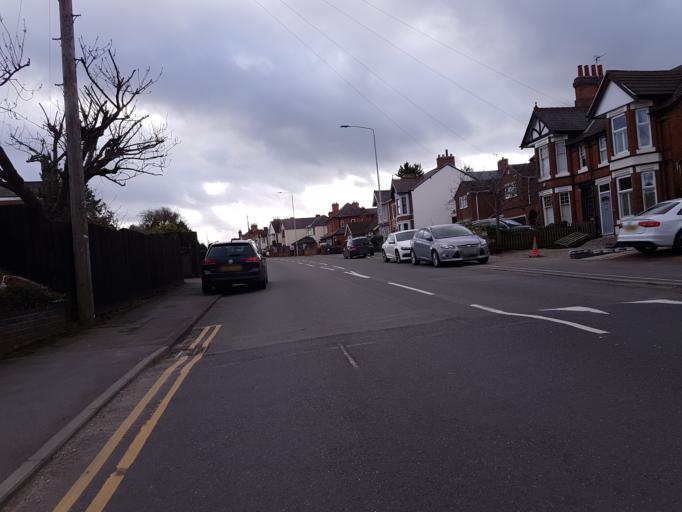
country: GB
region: England
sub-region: Leicestershire
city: Earl Shilton
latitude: 52.5735
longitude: -1.3247
